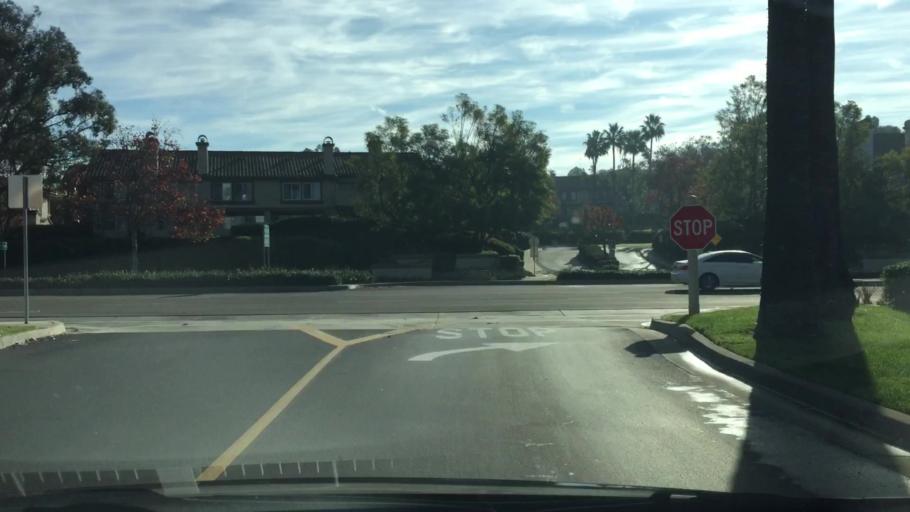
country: US
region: California
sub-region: Orange County
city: Rancho Santa Margarita
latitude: 33.6377
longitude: -117.5903
